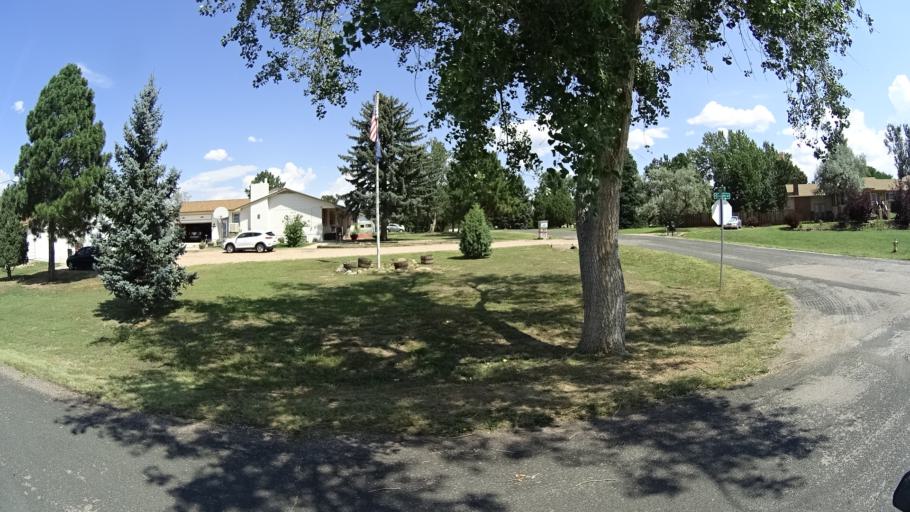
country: US
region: Colorado
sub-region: El Paso County
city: Air Force Academy
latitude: 38.9347
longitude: -104.7916
